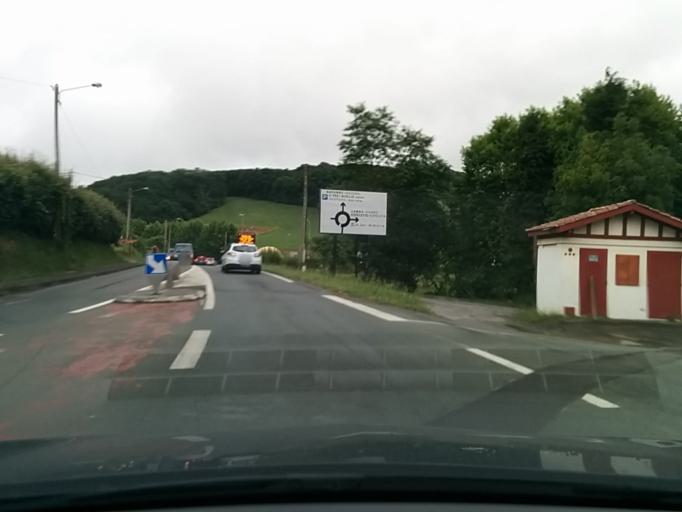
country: FR
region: Aquitaine
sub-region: Departement des Pyrenees-Atlantiques
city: Saint-Pee-sur-Nivelle
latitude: 43.3564
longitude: -1.5609
